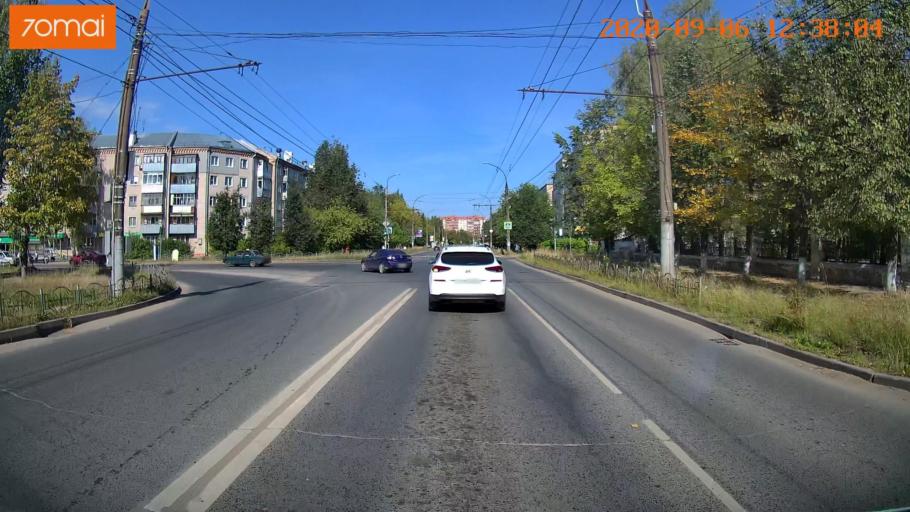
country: RU
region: Ivanovo
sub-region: Gorod Ivanovo
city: Ivanovo
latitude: 57.0302
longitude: 40.9805
